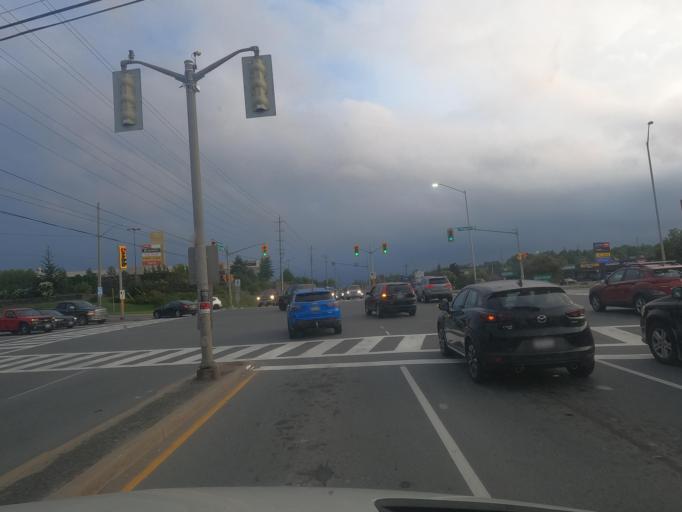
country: CA
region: Ontario
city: Greater Sudbury
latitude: 46.4517
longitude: -81.0030
